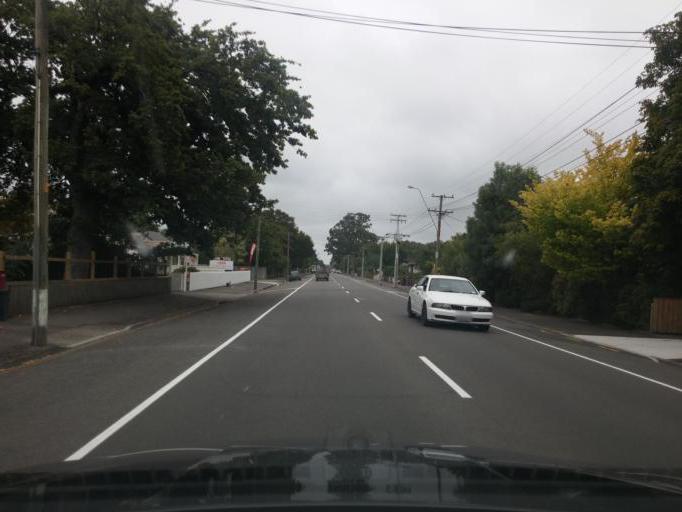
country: NZ
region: Wellington
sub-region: Masterton District
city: Masterton
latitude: -41.0848
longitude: 175.4554
